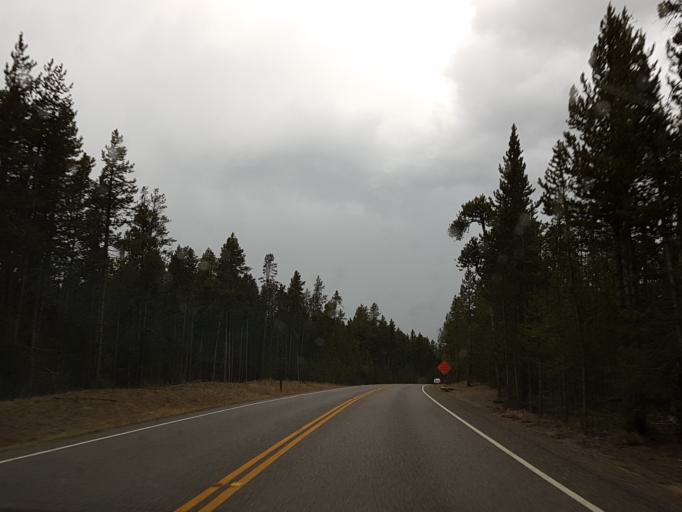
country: US
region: Montana
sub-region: Gallatin County
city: West Yellowstone
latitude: 44.4618
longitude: -110.5125
